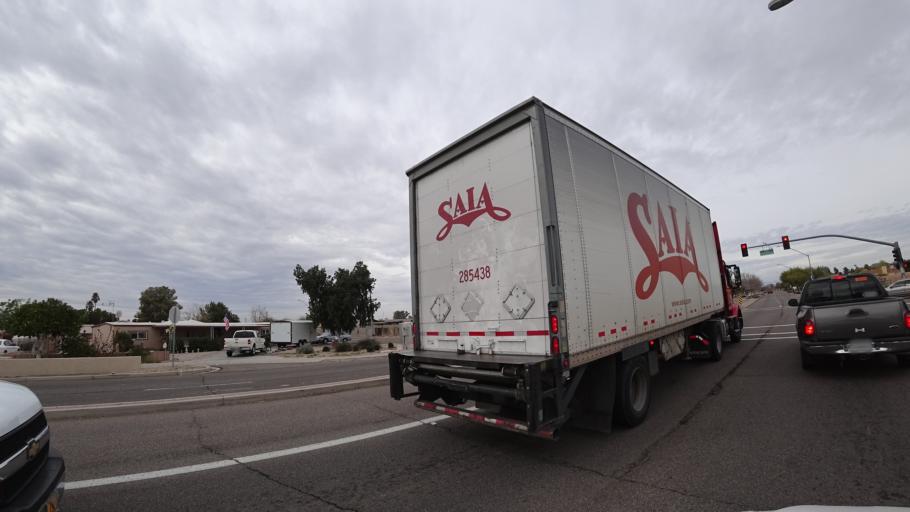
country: US
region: Arizona
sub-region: Maricopa County
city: Peoria
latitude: 33.6319
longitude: -112.2024
